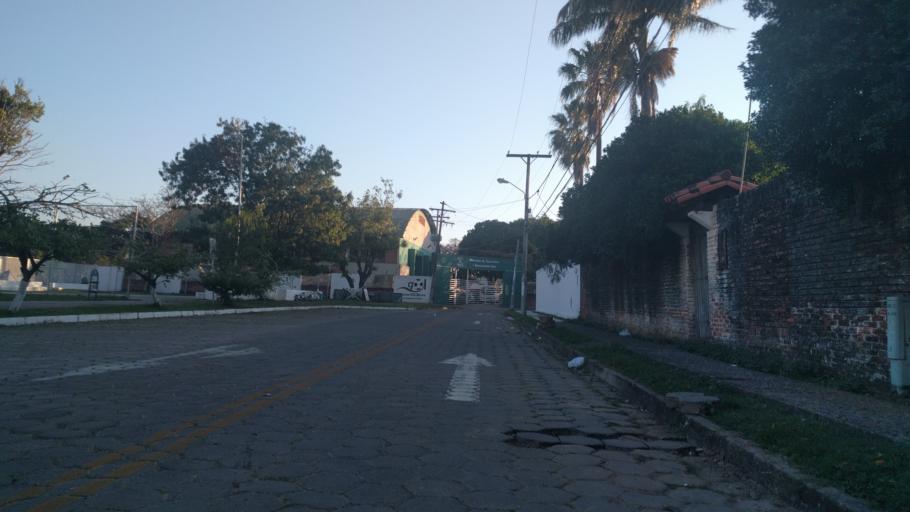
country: BO
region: Santa Cruz
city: Santa Cruz de la Sierra
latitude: -17.7966
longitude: -63.1988
